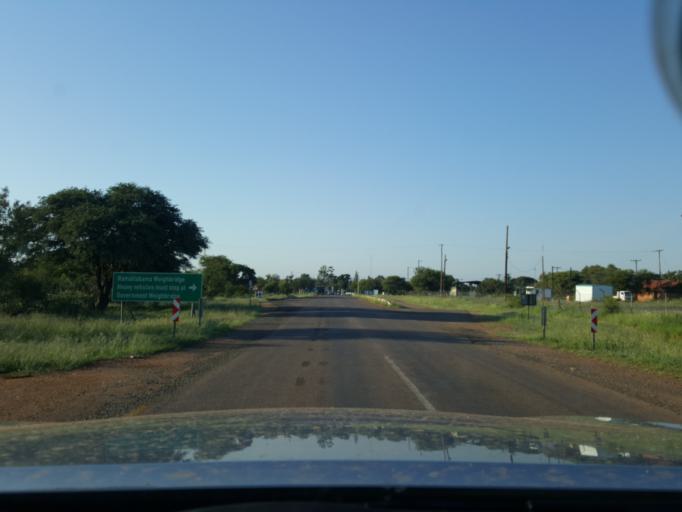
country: BW
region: South East
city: Janeng
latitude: -25.6349
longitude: 25.5741
